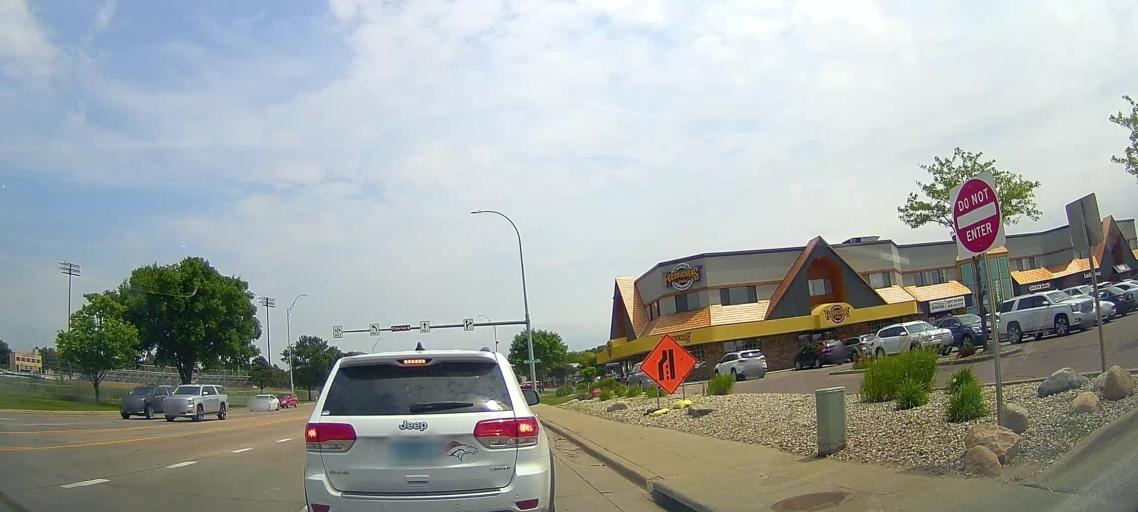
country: US
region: South Dakota
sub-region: Minnehaha County
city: Sioux Falls
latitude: 43.5147
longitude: -96.7643
